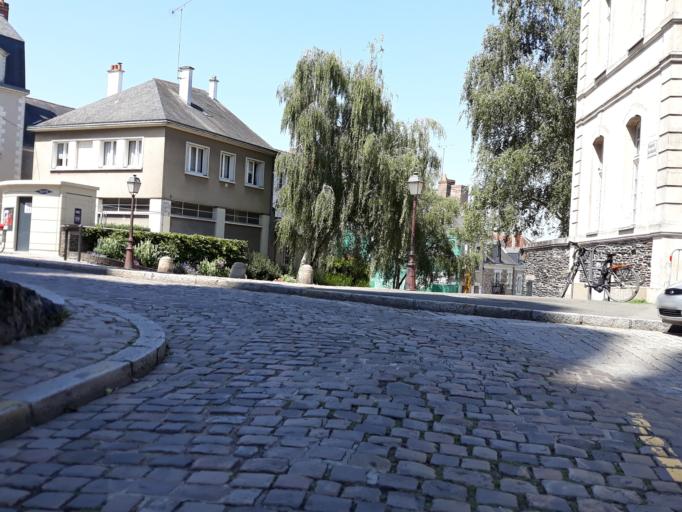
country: FR
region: Pays de la Loire
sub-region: Departement de Maine-et-Loire
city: Angers
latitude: 47.4711
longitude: -0.5554
